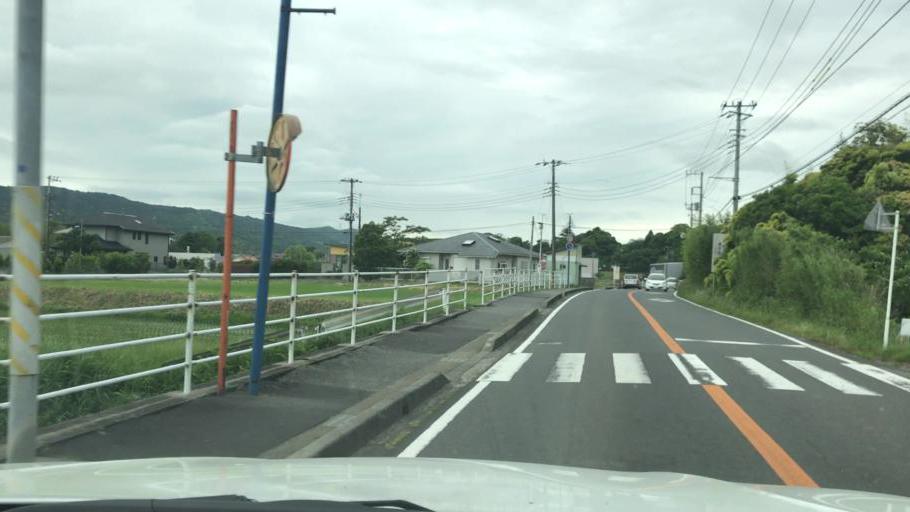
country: JP
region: Chiba
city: Kawaguchi
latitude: 35.1235
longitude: 140.0893
